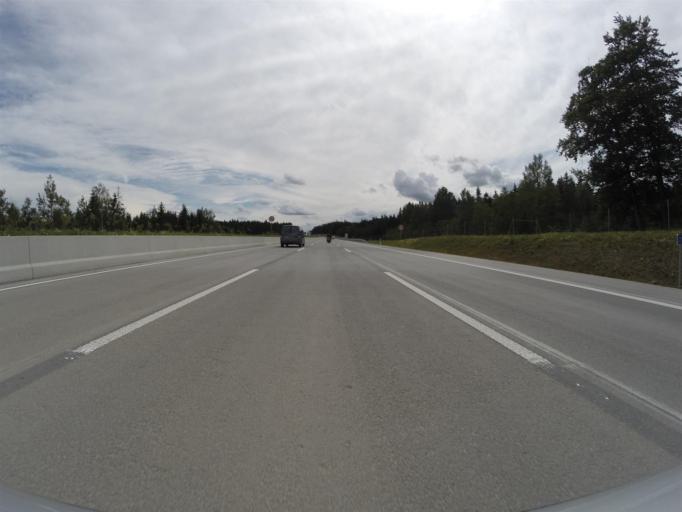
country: DE
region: Thuringia
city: Pormitz
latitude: 50.6267
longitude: 11.7944
